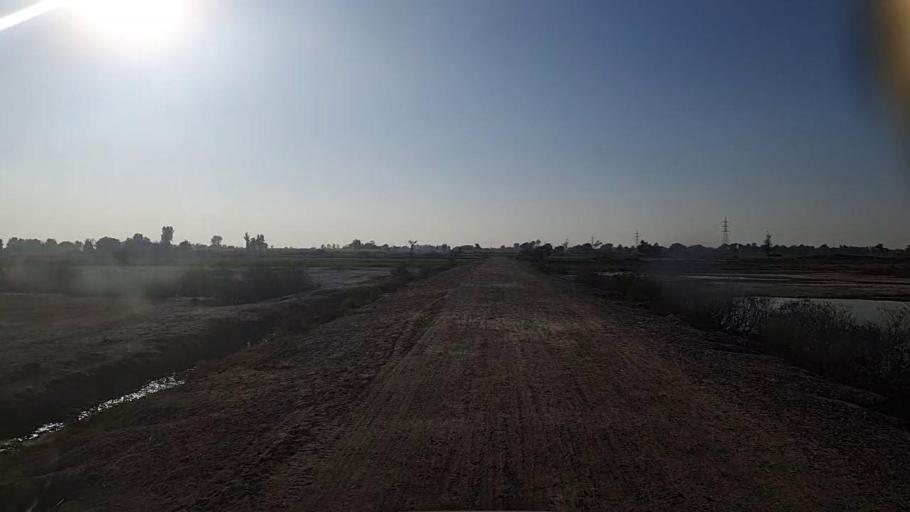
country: PK
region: Sindh
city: Khairpur
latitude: 28.0180
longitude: 69.7105
